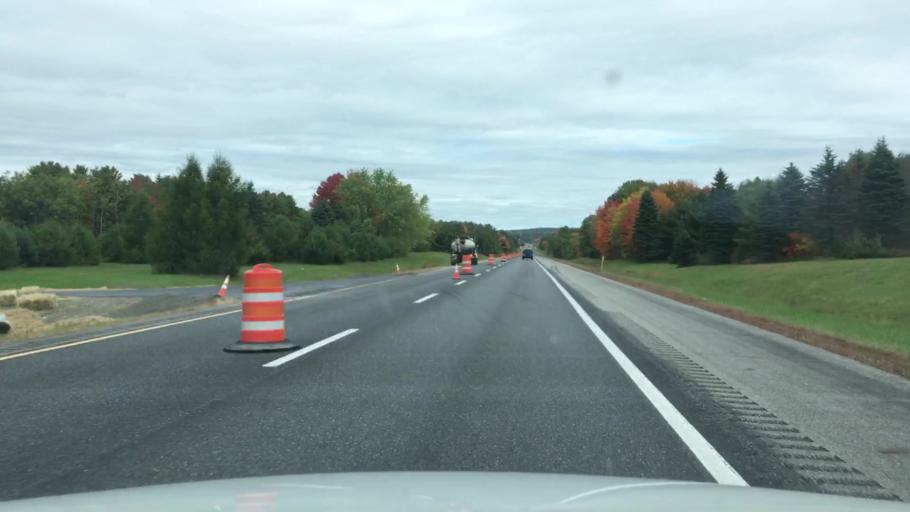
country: US
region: Maine
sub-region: Sagadahoc County
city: Richmond
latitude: 44.1289
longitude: -69.8468
